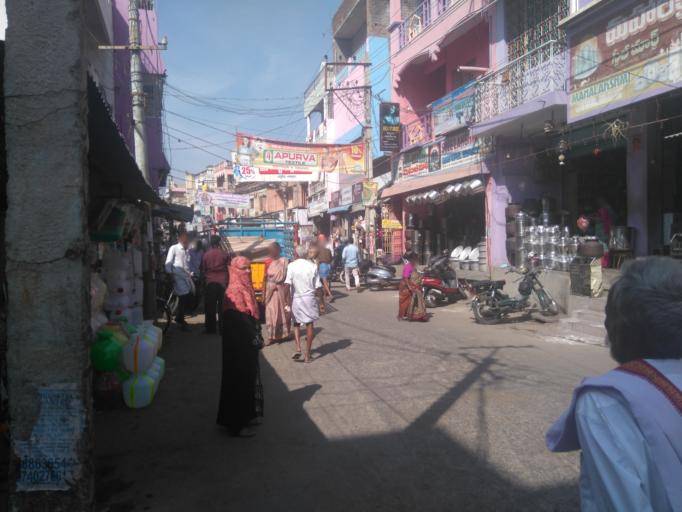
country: IN
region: Andhra Pradesh
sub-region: Chittoor
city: Chittoor
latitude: 13.2193
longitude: 79.0988
